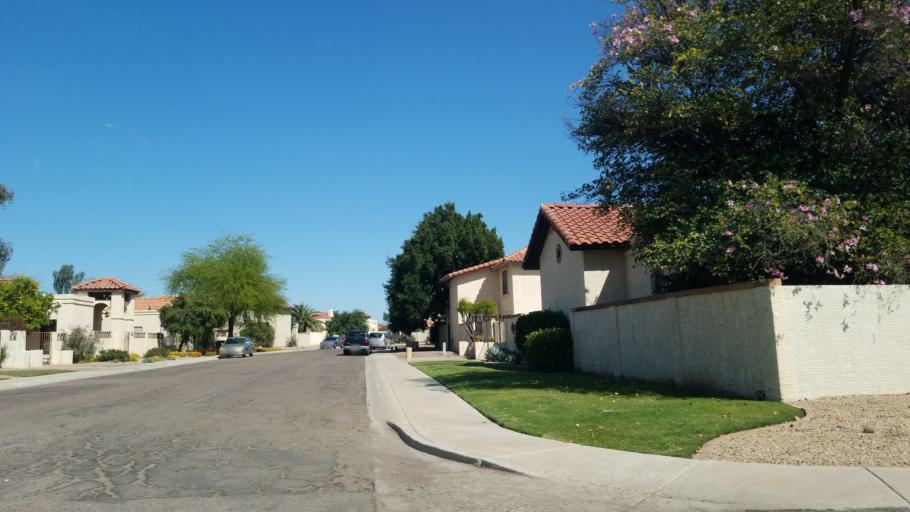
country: US
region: Arizona
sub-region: Maricopa County
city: Glendale
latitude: 33.5776
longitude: -112.1775
